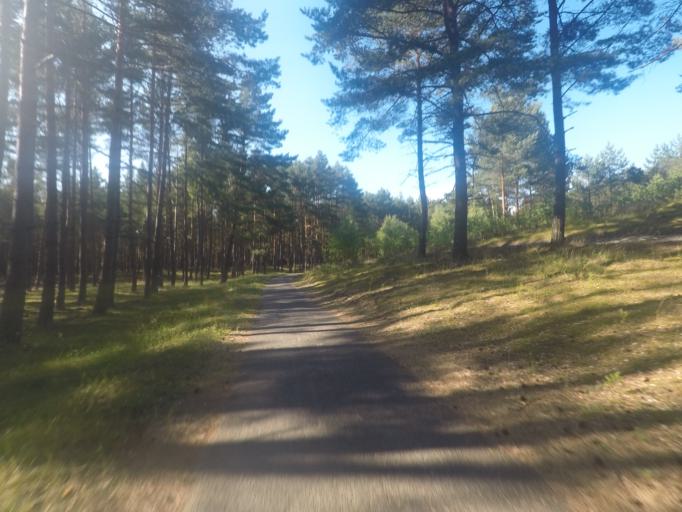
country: LT
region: Klaipedos apskritis
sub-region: Klaipeda
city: Klaipeda
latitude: 55.5803
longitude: 21.1135
